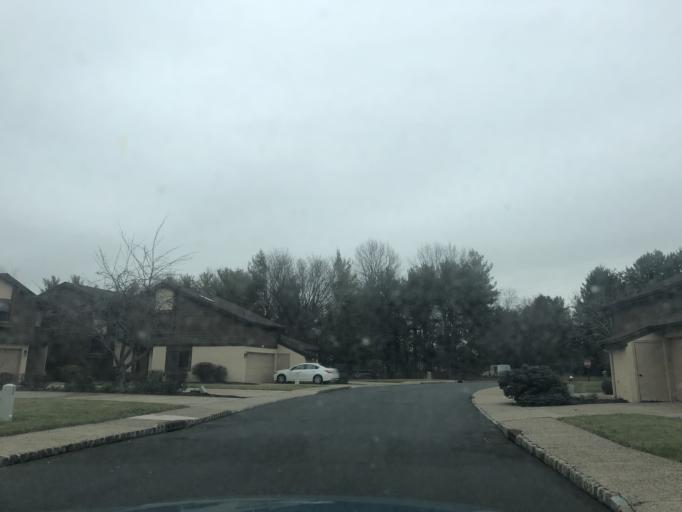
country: US
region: New Jersey
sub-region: Somerset County
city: Kingston
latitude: 40.3533
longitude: -74.6208
